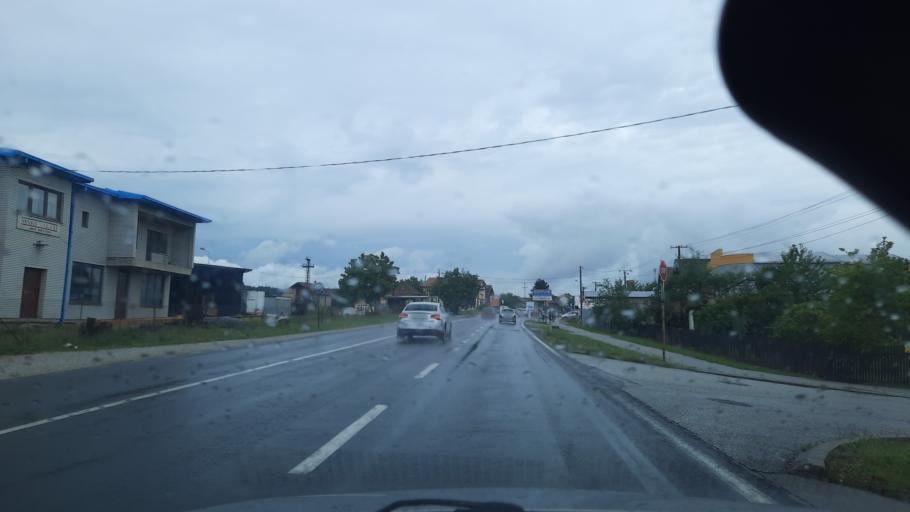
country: RS
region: Central Serbia
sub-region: Sumadijski Okrug
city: Kragujevac
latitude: 43.9913
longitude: 20.8588
